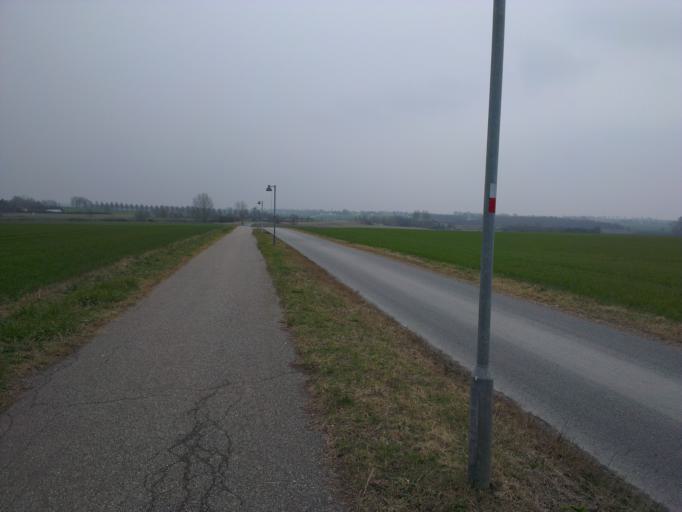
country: DK
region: Capital Region
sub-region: Frederikssund Kommune
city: Frederikssund
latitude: 55.8192
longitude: 12.0991
